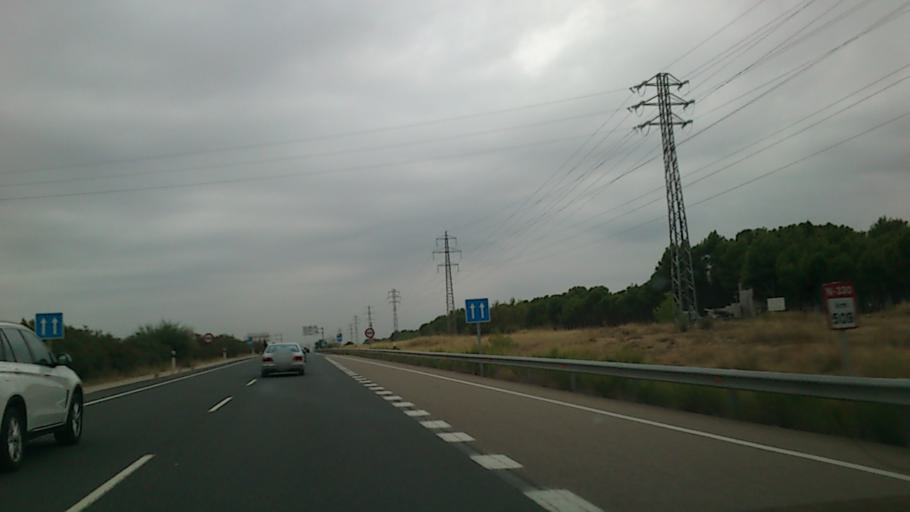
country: ES
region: Aragon
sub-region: Provincia de Zaragoza
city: Villanueva de Gallego
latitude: 41.7279
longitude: -0.8514
